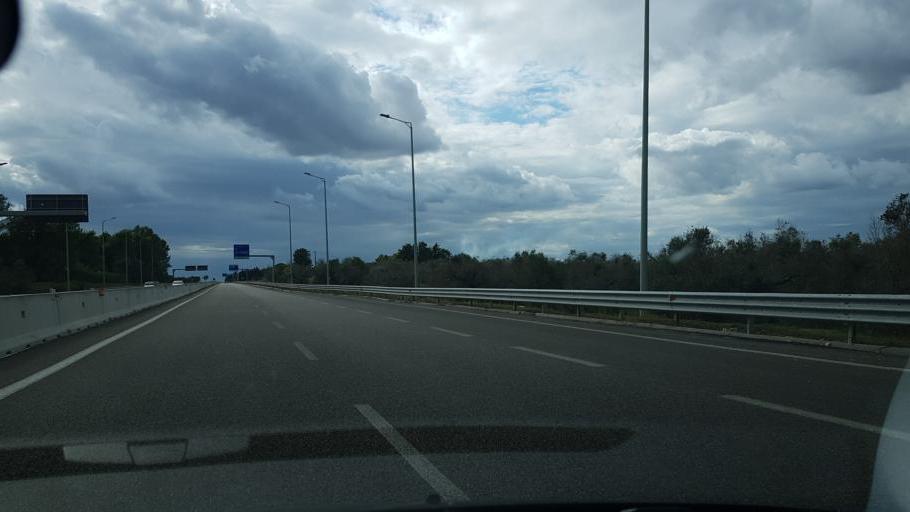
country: IT
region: Apulia
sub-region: Provincia di Lecce
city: Palmariggi
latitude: 40.1282
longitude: 18.3652
